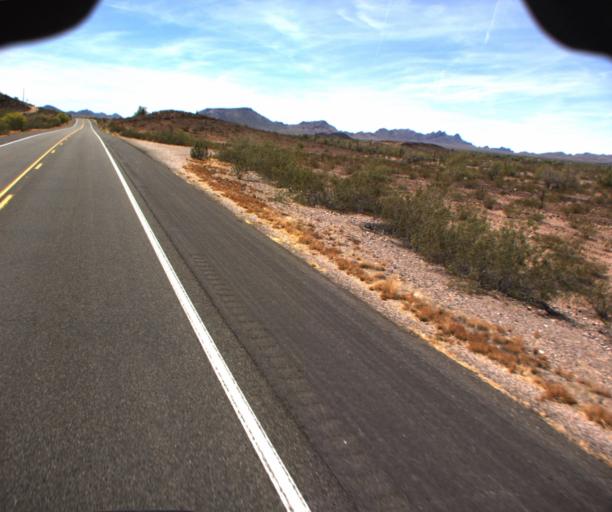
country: US
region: Arizona
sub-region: La Paz County
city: Quartzsite
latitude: 33.6840
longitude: -113.9289
